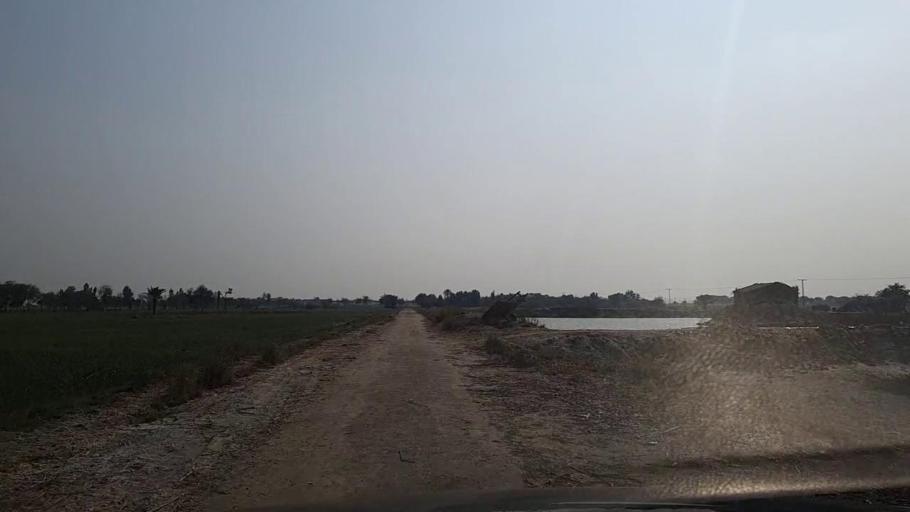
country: PK
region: Sindh
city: Daur
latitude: 26.4037
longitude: 68.4201
